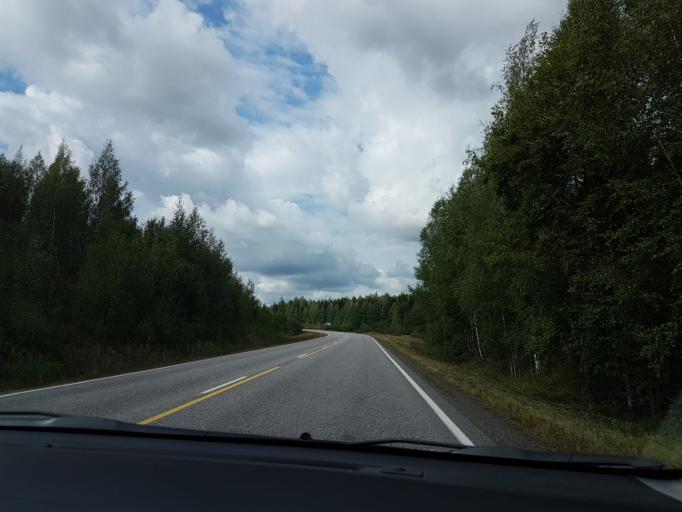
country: FI
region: Uusimaa
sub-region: Helsinki
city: Pornainen
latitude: 60.4774
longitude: 25.3243
